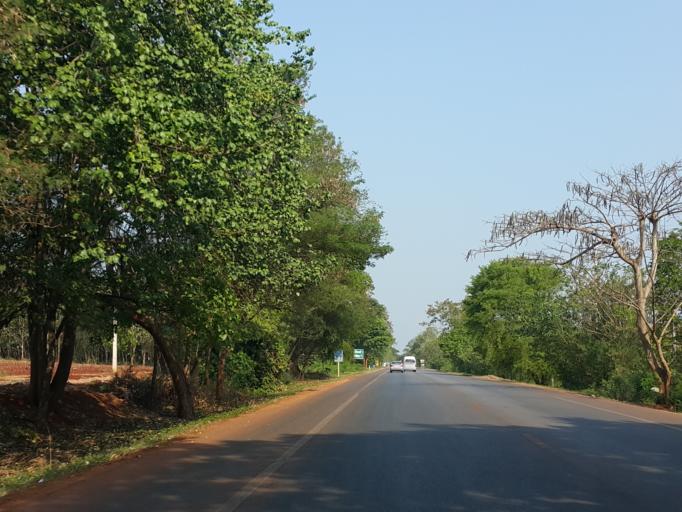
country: TH
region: Kanchanaburi
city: Sai Yok
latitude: 14.1201
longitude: 99.1824
